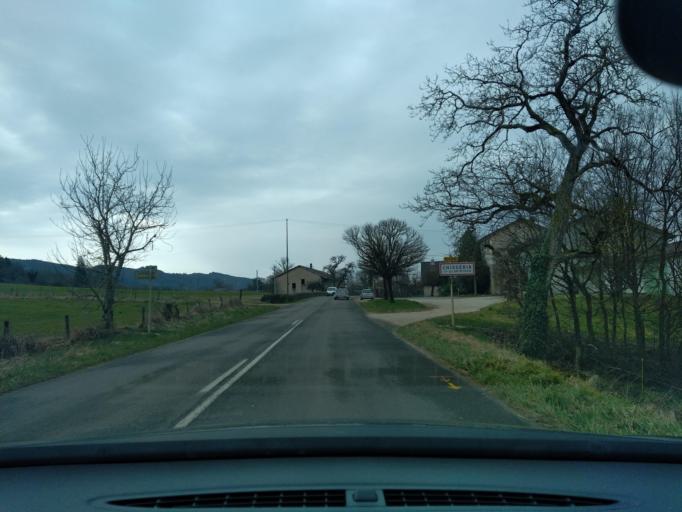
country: FR
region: Franche-Comte
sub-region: Departement du Jura
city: Arinthod
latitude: 46.3822
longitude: 5.5644
